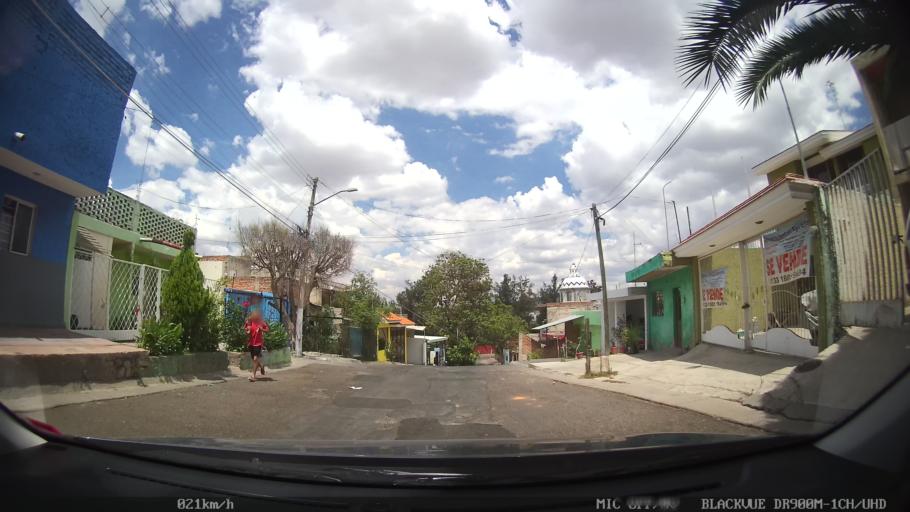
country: MX
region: Jalisco
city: Tlaquepaque
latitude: 20.6500
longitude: -103.2743
